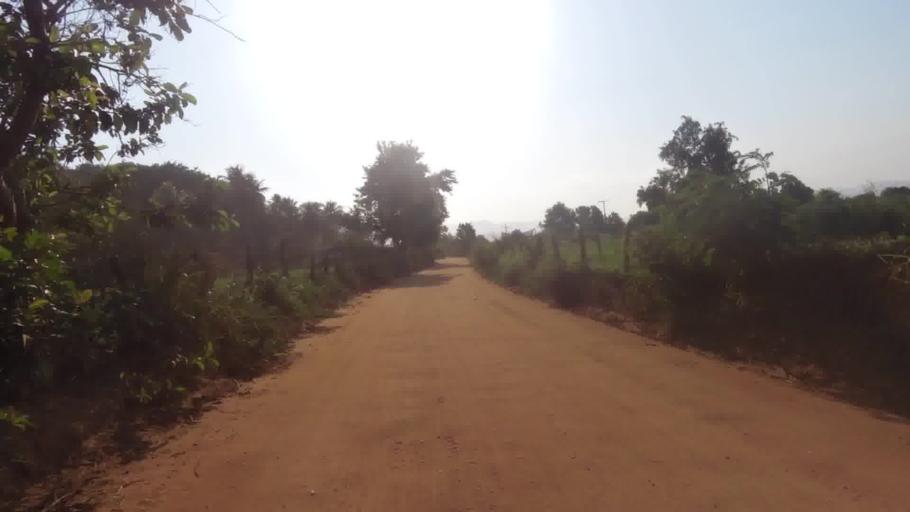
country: BR
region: Espirito Santo
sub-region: Piuma
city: Piuma
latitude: -20.8540
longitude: -40.7572
